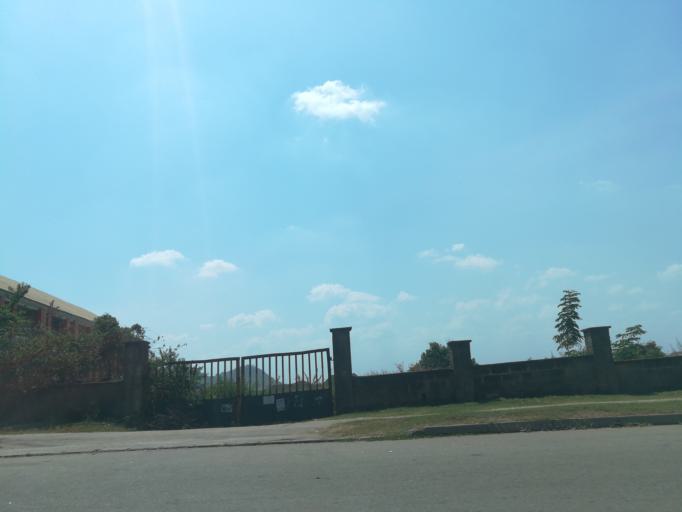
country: NG
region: Abuja Federal Capital Territory
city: Abuja
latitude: 9.0607
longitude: 7.4478
